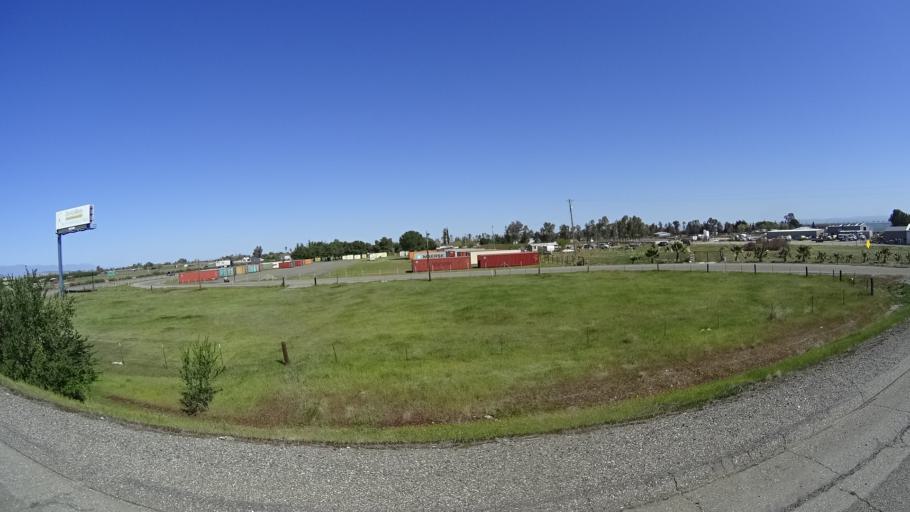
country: US
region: California
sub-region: Glenn County
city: Orland
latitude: 39.7007
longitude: -122.1976
